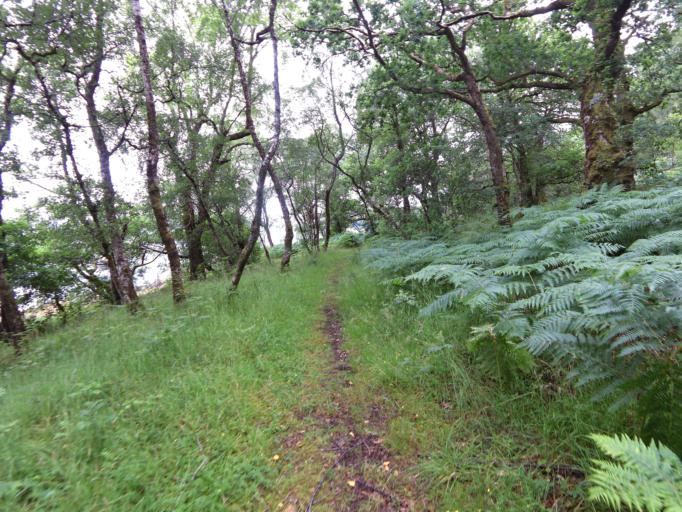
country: GB
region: Scotland
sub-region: Highland
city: Fort William
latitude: 56.8325
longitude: -5.1236
